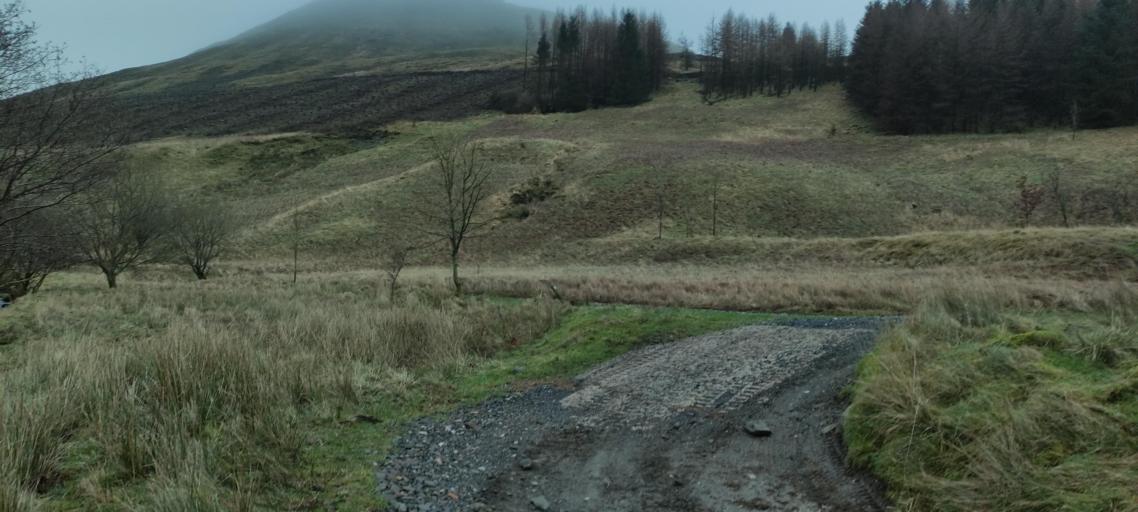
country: GB
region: England
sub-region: Cumbria
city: Kendal
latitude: 54.4268
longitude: -2.6873
